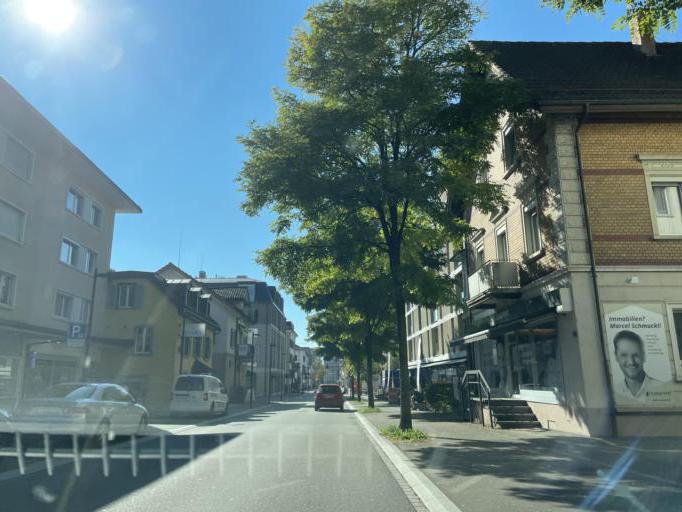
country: CH
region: Zurich
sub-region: Bezirk Uster
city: Uster
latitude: 47.3509
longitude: 8.7209
